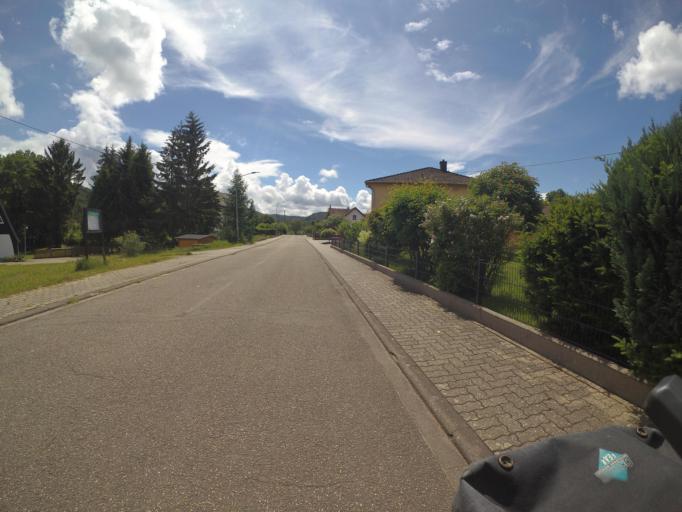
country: DE
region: Rheinland-Pfalz
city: Ludwigswinkel
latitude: 49.0809
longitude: 7.6703
